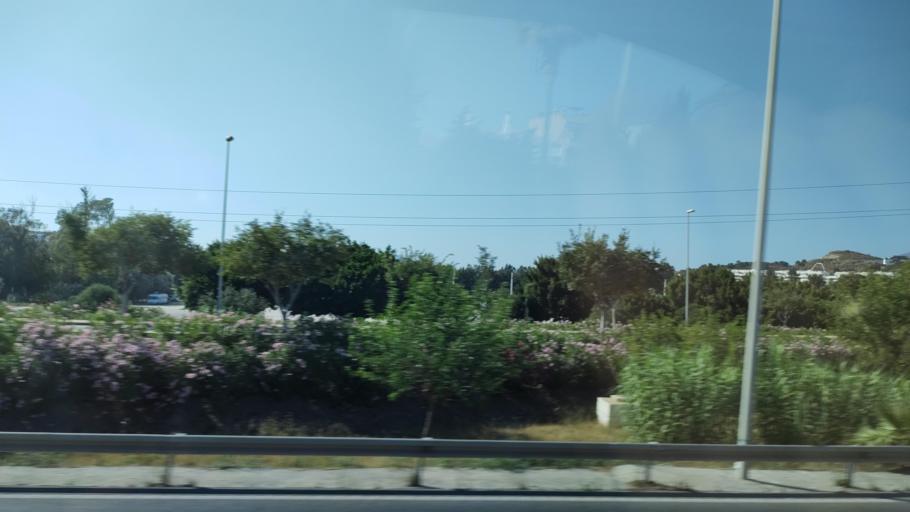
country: ES
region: Andalusia
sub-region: Provincia de Malaga
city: Fuengirola
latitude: 36.5032
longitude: -4.6827
